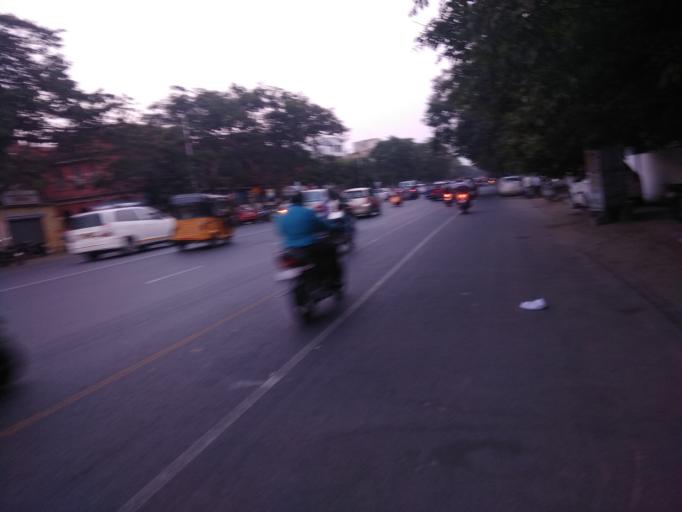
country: IN
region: Tamil Nadu
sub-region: Kancheepuram
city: Alandur
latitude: 13.0137
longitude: 80.2264
